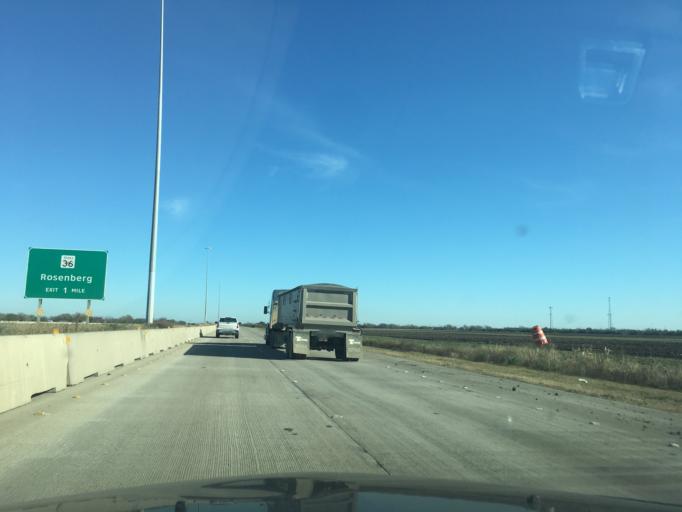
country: US
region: Texas
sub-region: Fort Bend County
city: Rosenberg
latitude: 29.5332
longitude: -95.8387
